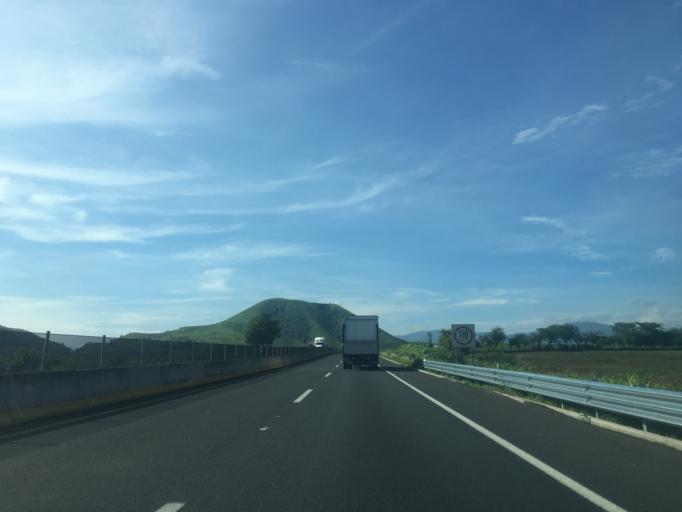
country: MX
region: Nayarit
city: Jala
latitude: 21.0680
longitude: -104.4186
